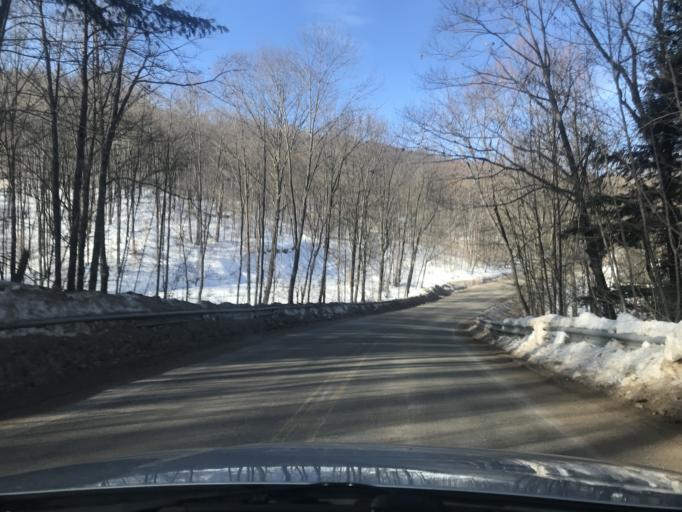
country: US
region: Michigan
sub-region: Dickinson County
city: Kingsford
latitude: 45.4024
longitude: -88.3436
